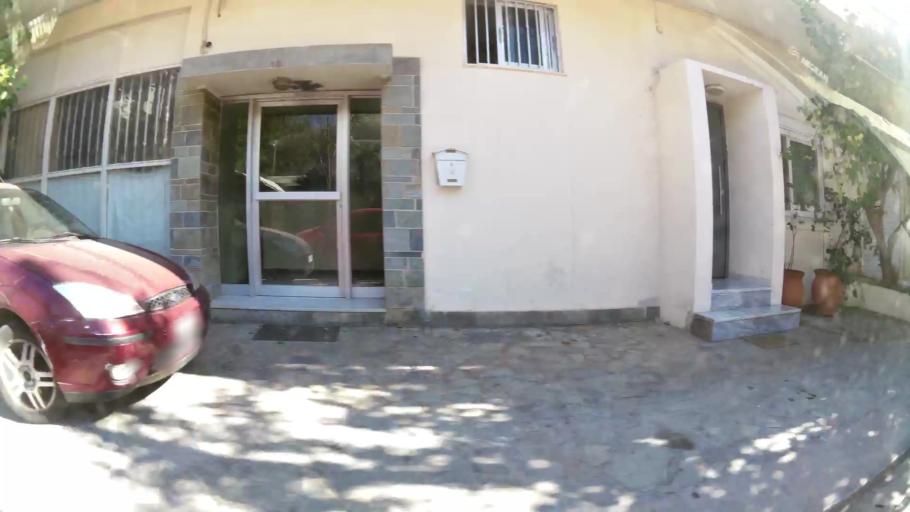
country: GR
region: Attica
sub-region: Nomarchia Anatolikis Attikis
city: Pikermi
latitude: 38.0023
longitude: 23.9385
